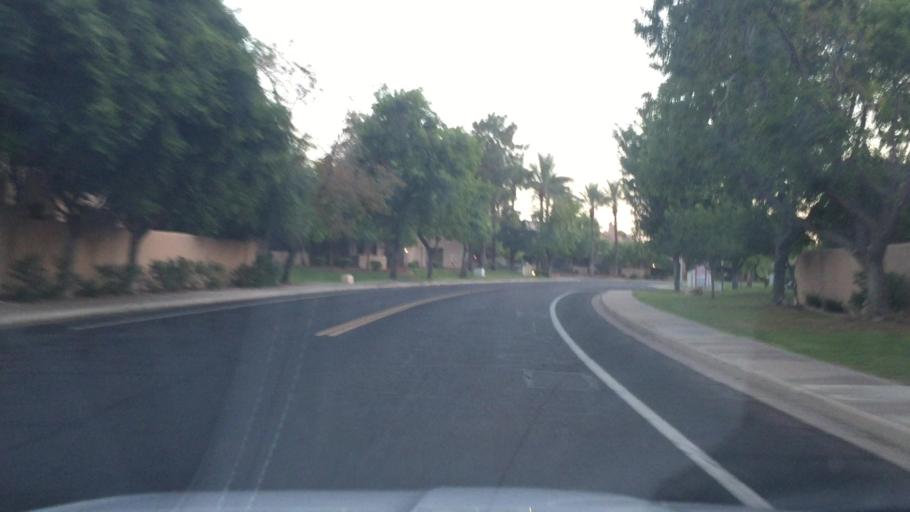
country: US
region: Arizona
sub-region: Maricopa County
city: Scottsdale
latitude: 33.5210
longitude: -111.9135
